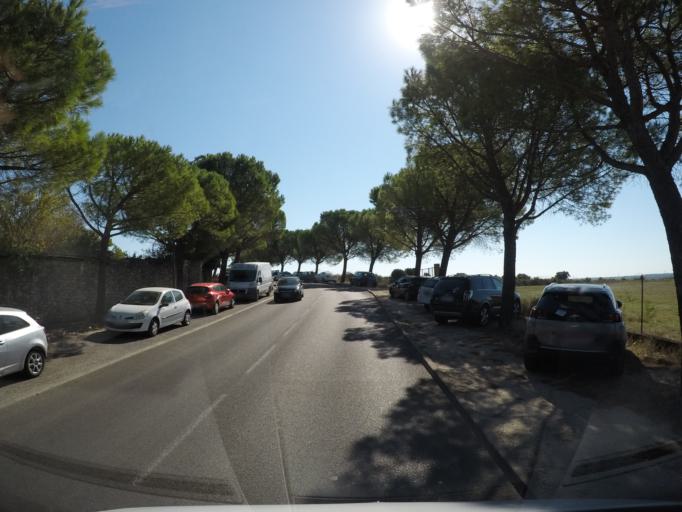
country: FR
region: Languedoc-Roussillon
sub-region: Departement du Gard
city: Uzes
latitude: 44.0078
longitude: 4.4152
